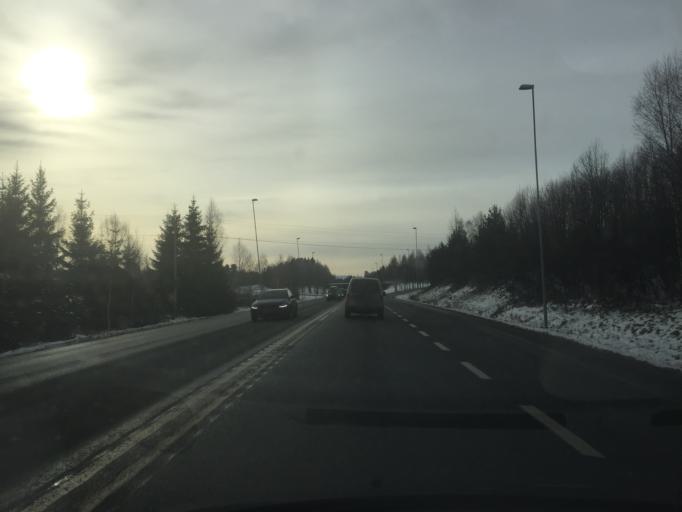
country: NO
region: Hedmark
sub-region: Loten
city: Loten
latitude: 60.7332
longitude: 11.2971
